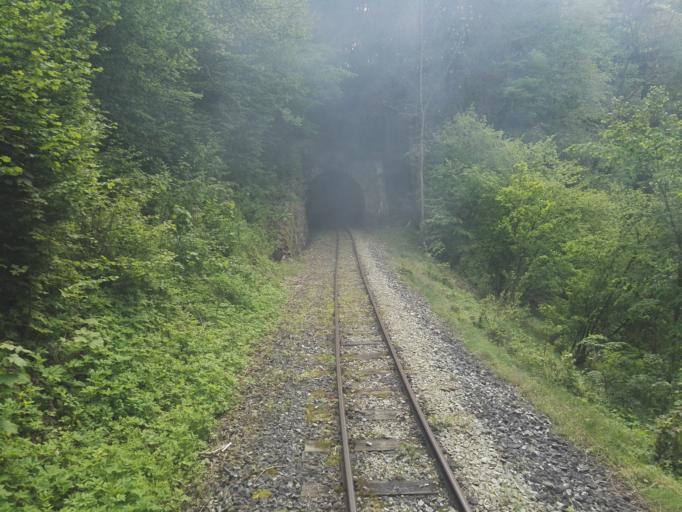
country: AT
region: Styria
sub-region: Politischer Bezirk Weiz
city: Koglhof
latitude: 47.3138
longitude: 15.6924
